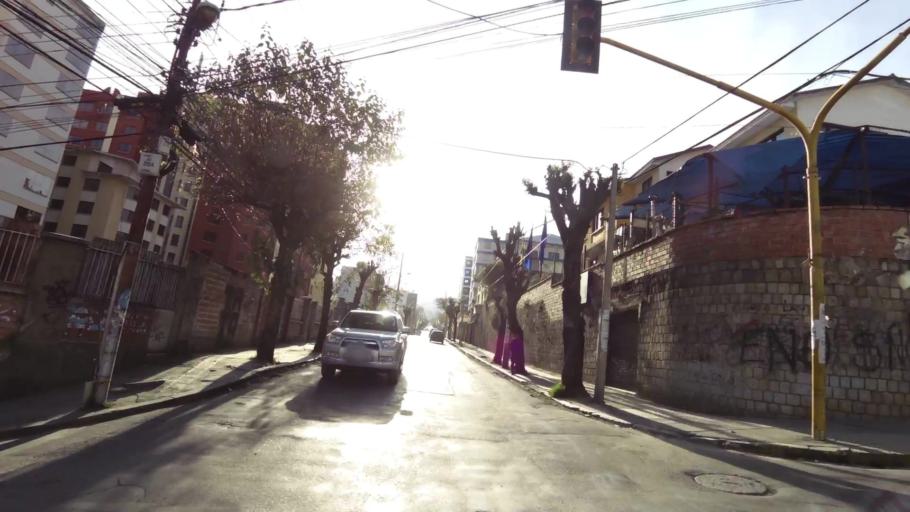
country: BO
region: La Paz
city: La Paz
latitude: -16.5262
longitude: -68.1065
